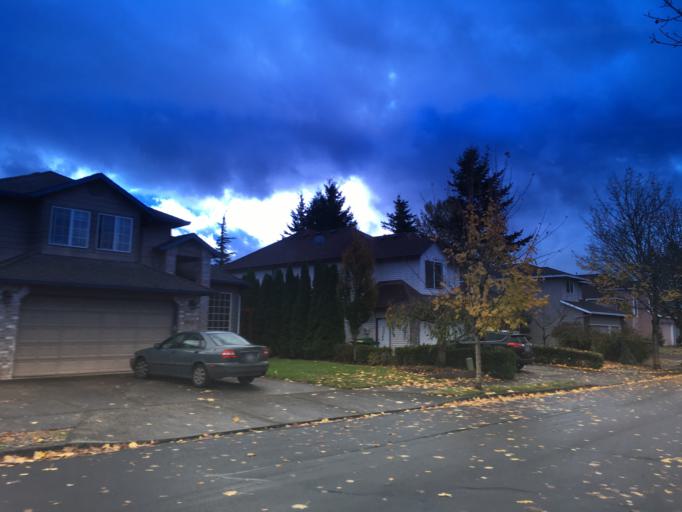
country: US
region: Oregon
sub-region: Multnomah County
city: Troutdale
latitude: 45.5207
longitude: -122.3936
